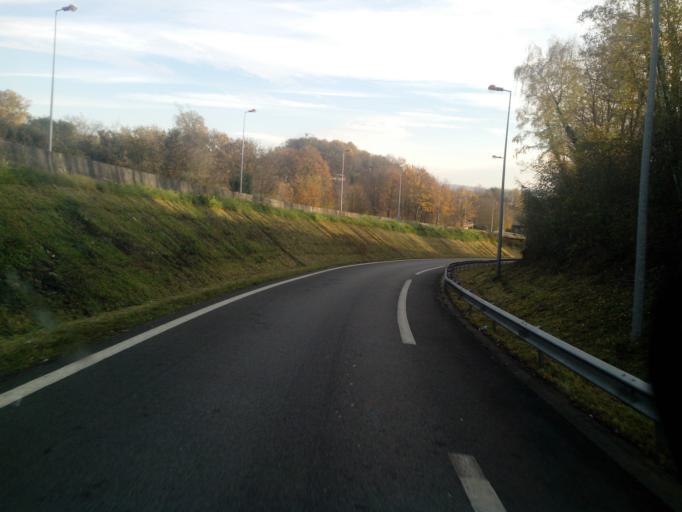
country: FR
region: Limousin
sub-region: Departement de la Haute-Vienne
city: Limoges
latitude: 45.8514
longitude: 1.2744
